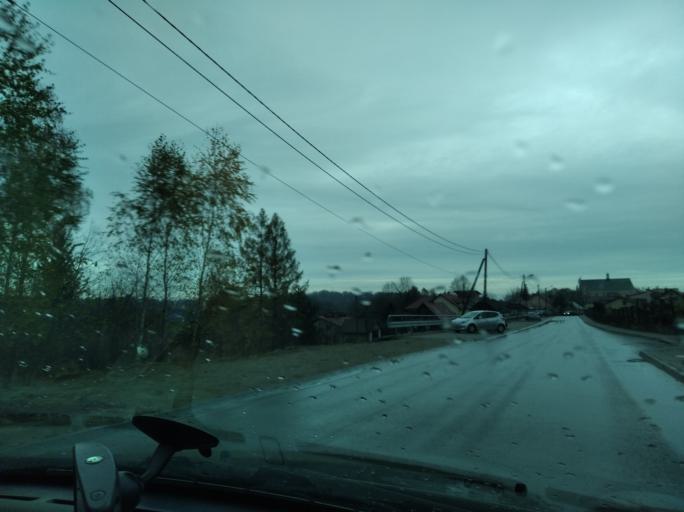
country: PL
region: Subcarpathian Voivodeship
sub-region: Powiat rzeszowski
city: Tyczyn
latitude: 49.9579
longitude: 22.0363
